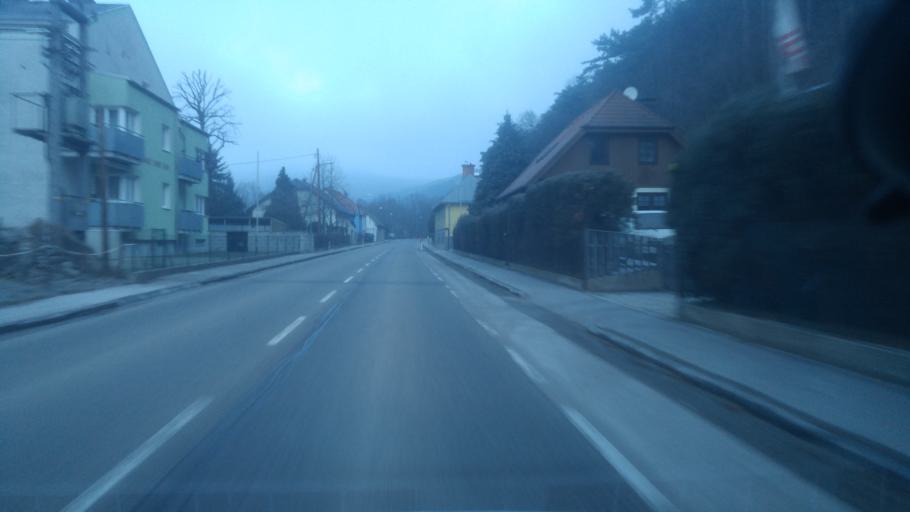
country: AT
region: Lower Austria
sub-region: Politischer Bezirk Baden
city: Pottenstein
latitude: 47.9743
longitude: 16.0711
